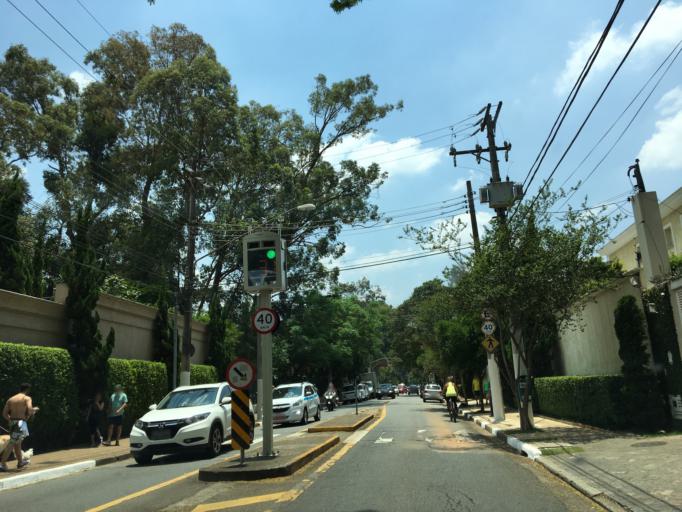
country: BR
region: Sao Paulo
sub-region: Sao Paulo
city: Sao Paulo
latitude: -23.5943
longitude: -46.6614
